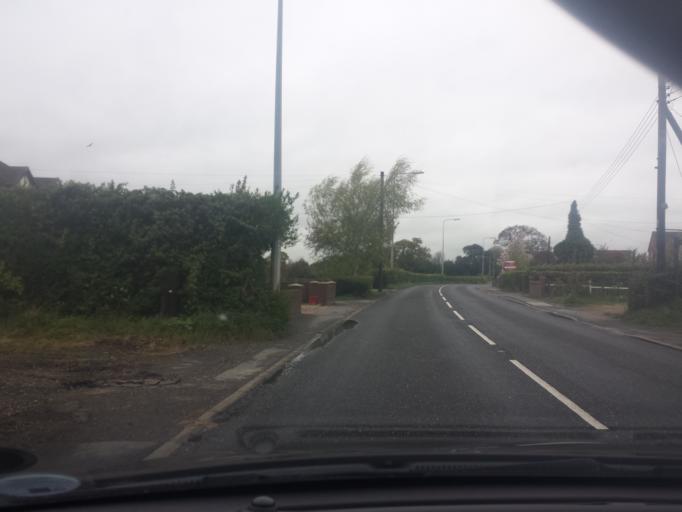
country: GB
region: England
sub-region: Essex
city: Little Clacton
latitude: 51.8312
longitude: 1.1397
